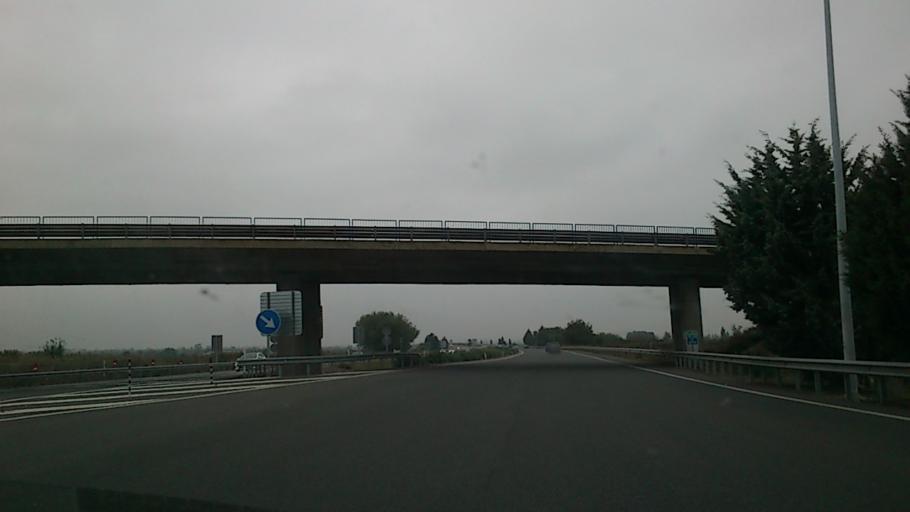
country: ES
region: Aragon
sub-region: Provincia de Zaragoza
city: Alagon
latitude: 41.7776
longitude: -1.1258
